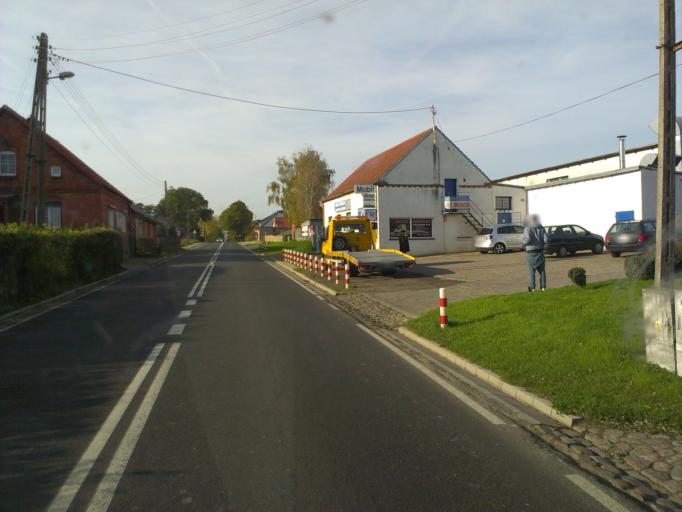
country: PL
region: West Pomeranian Voivodeship
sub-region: Powiat pyrzycki
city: Kozielice
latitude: 53.1308
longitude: 14.8327
